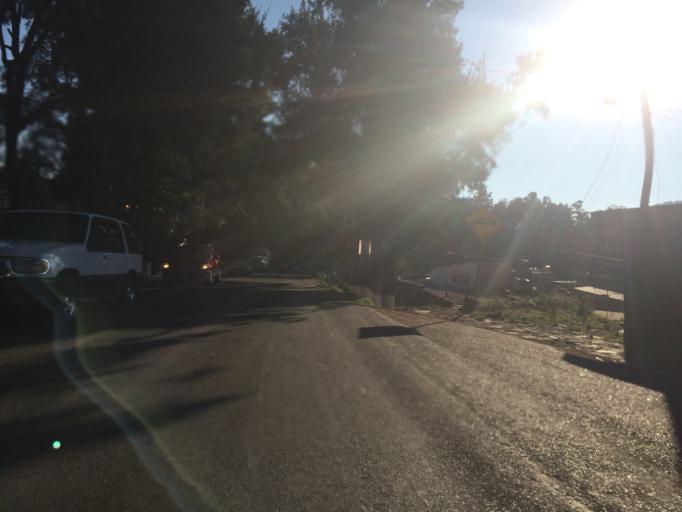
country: MX
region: Michoacan
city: Patzcuaro
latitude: 19.5061
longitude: -101.6117
